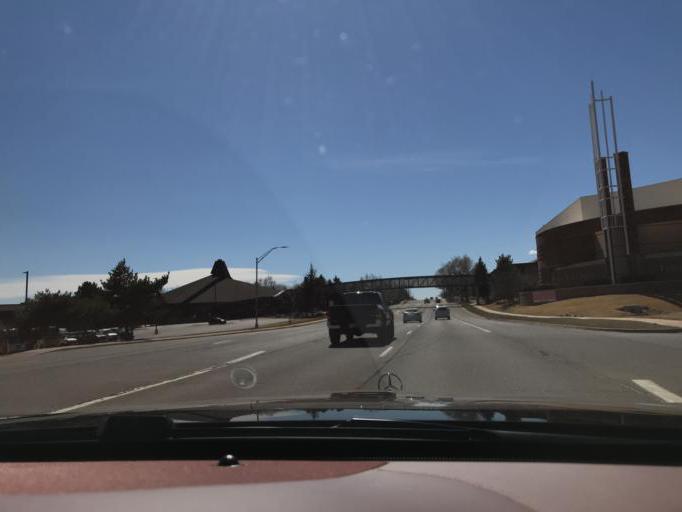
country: US
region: Colorado
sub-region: Jefferson County
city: Arvada
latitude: 39.8114
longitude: -105.1380
